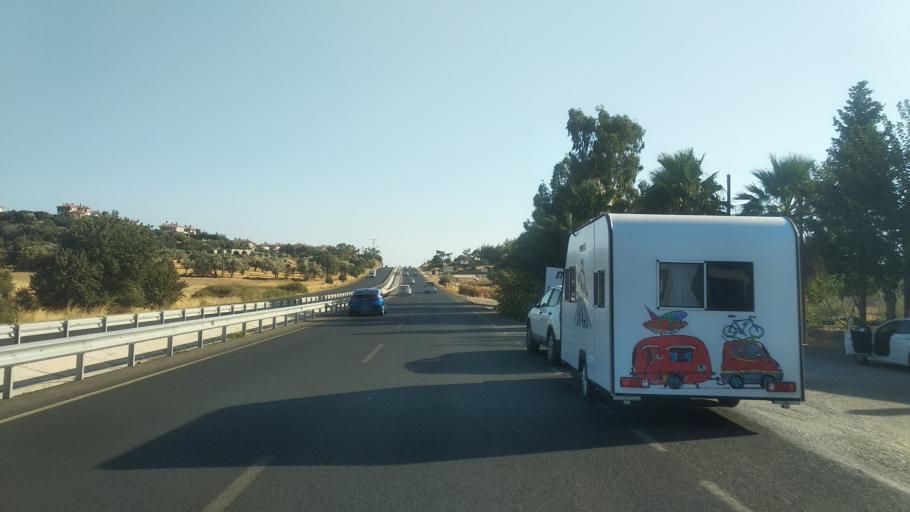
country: TR
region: Izmir
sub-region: Seferihisar
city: Seferhisar
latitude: 38.2614
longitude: 26.8332
